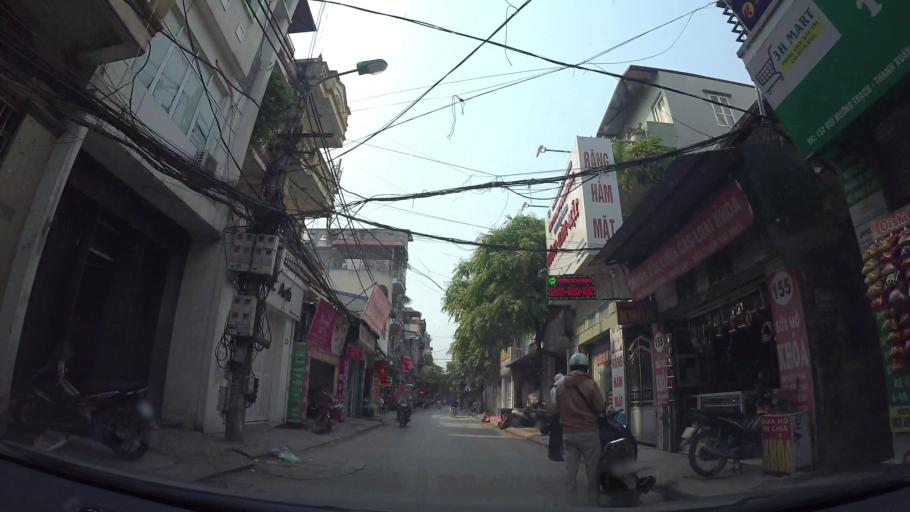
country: VN
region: Ha Noi
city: Thanh Xuan
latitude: 20.9882
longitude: 105.8183
